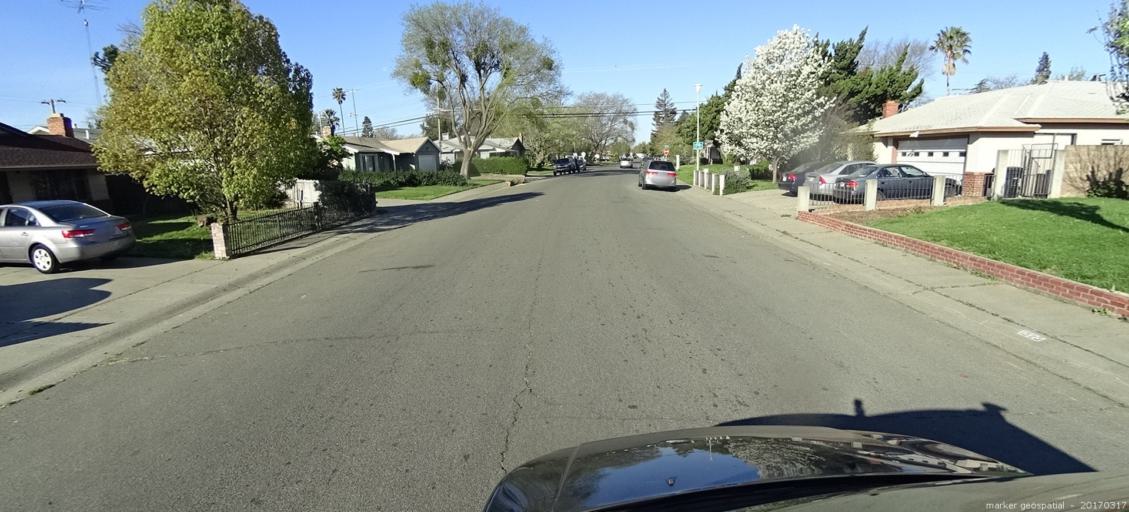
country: US
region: California
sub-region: Sacramento County
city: Parkway
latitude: 38.4915
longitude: -121.5009
